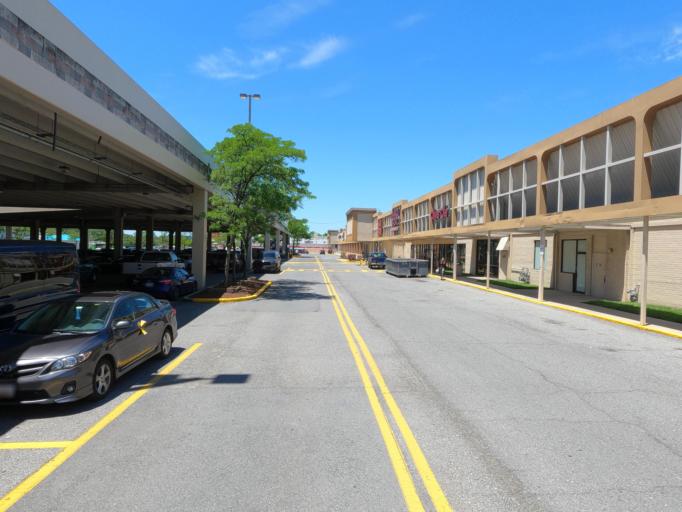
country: US
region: Maryland
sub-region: Prince George's County
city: Berwyn Heights
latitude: 38.9988
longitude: -76.9078
